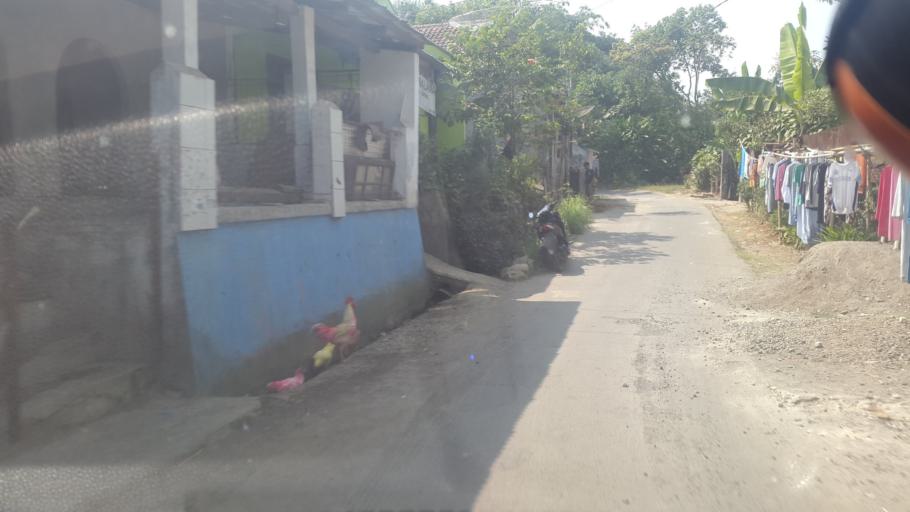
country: ID
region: West Java
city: Cicurug
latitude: -6.7721
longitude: 106.7542
